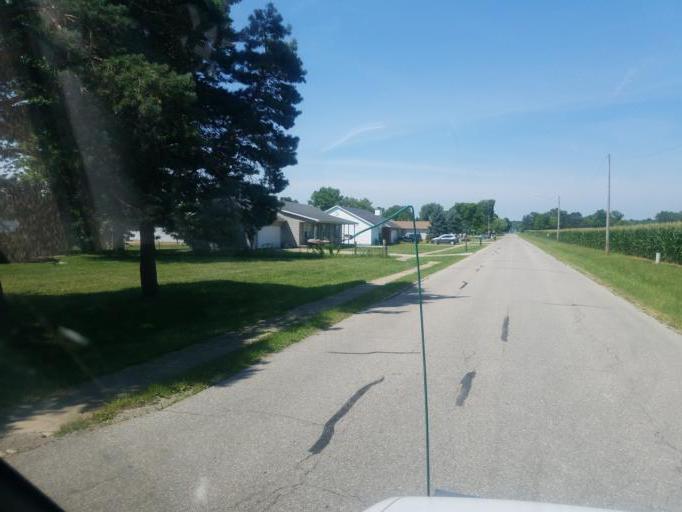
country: US
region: Ohio
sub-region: Champaign County
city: North Lewisburg
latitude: 40.2273
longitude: -83.5610
